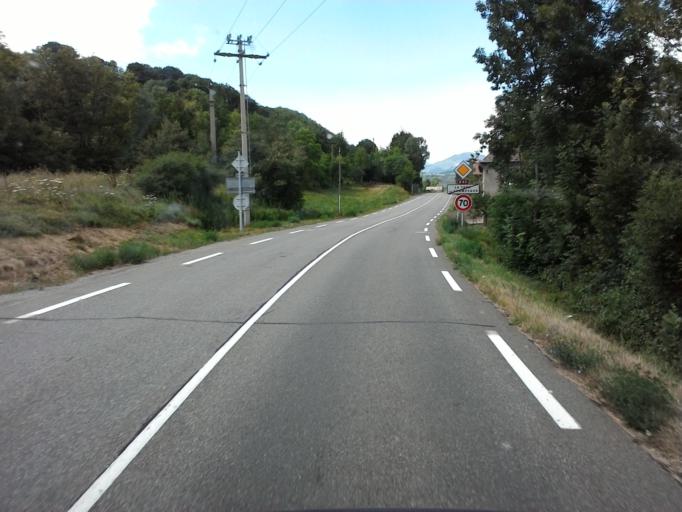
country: FR
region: Provence-Alpes-Cote d'Azur
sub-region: Departement des Hautes-Alpes
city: Saint-Bonnet-en-Champsaur
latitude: 44.6796
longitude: 6.0684
